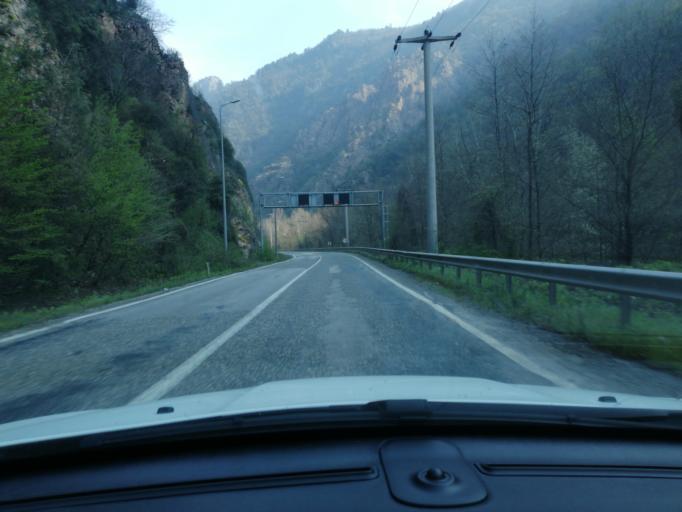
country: TR
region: Karabuk
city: Yenice
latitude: 41.1782
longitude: 32.4475
